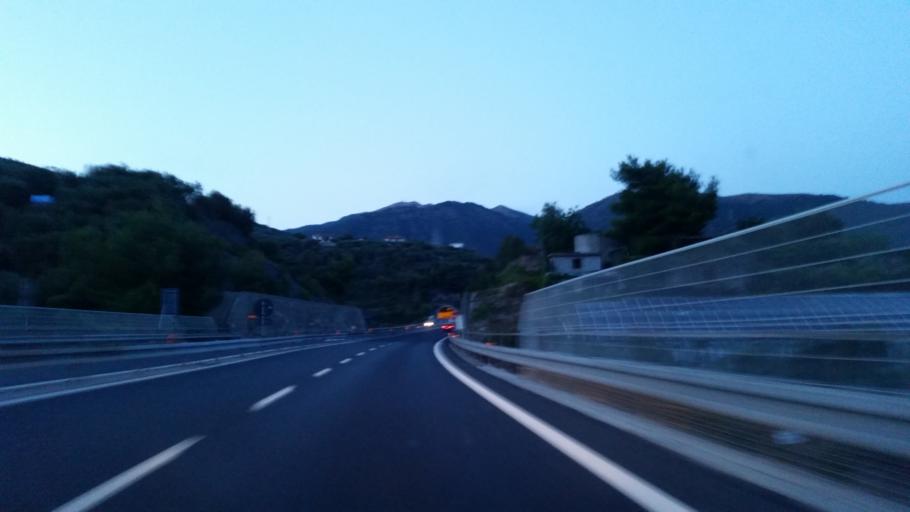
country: IT
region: Liguria
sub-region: Provincia di Imperia
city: Taggia
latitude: 43.8549
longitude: 7.8402
